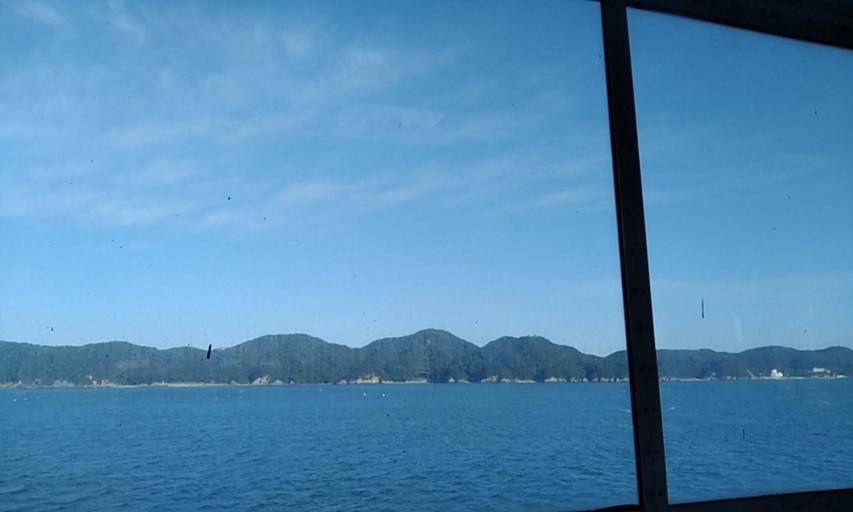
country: JP
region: Mie
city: Toba
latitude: 34.5034
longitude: 136.8834
